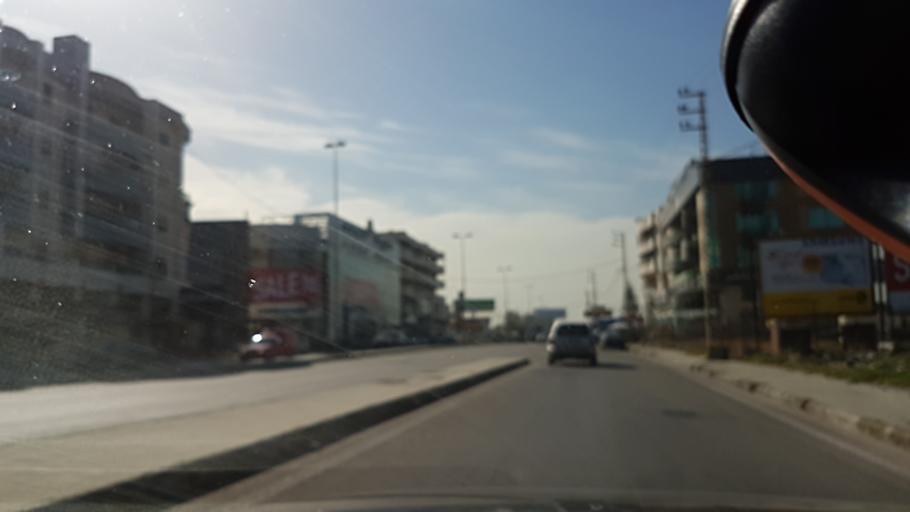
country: LB
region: Liban-Sud
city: Sidon
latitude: 33.5857
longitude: 35.3875
